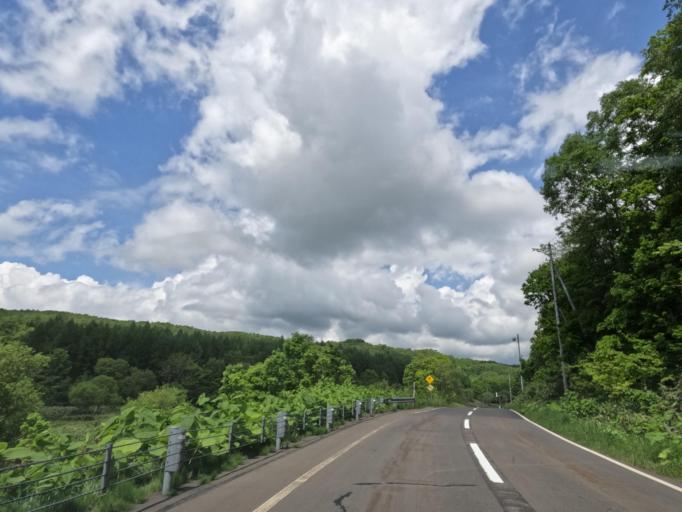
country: JP
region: Hokkaido
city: Takikawa
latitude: 43.5492
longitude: 141.6522
